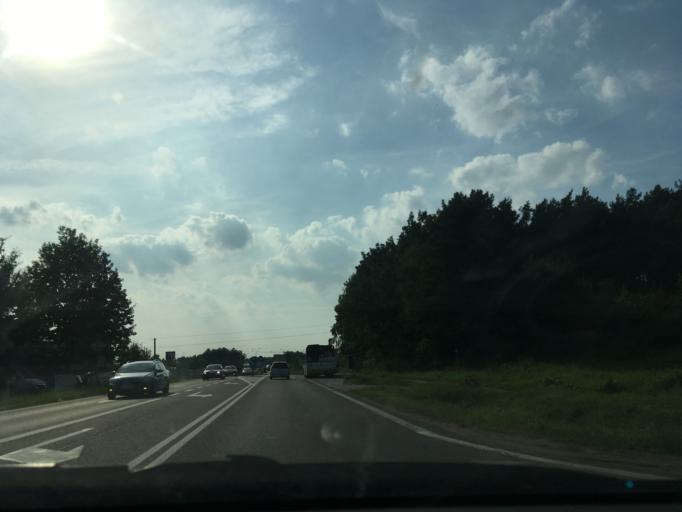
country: PL
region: Podlasie
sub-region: Bialystok
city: Bialystok
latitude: 53.1258
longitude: 23.2395
